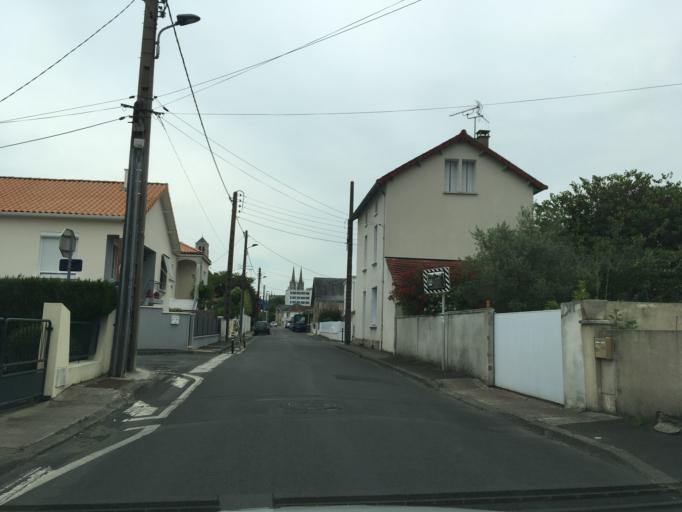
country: FR
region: Poitou-Charentes
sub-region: Departement des Deux-Sevres
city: Niort
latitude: 46.3272
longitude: -0.4728
